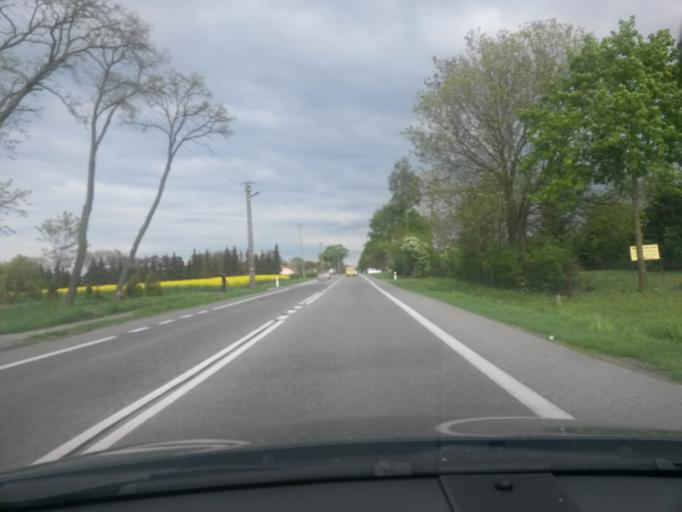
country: PL
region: Masovian Voivodeship
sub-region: Powiat plonski
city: Dzierzaznia
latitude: 52.6279
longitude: 20.2333
